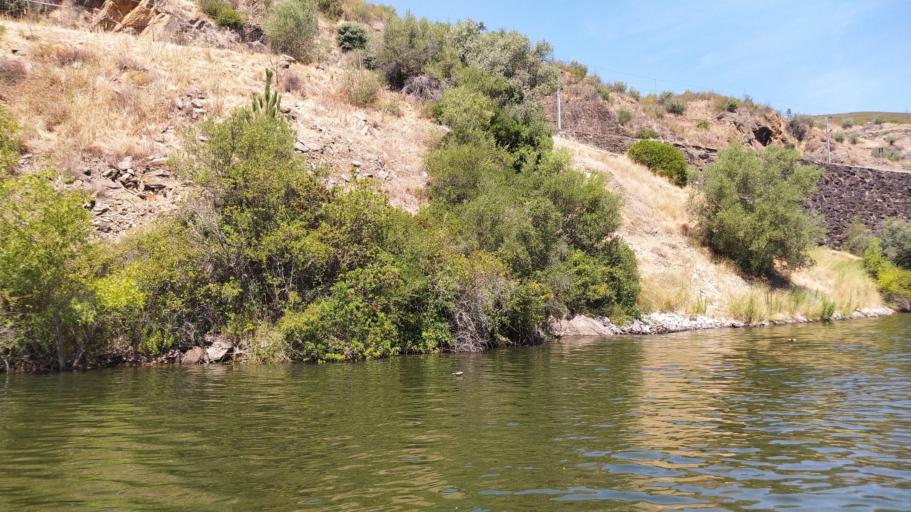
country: PT
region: Portalegre
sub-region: Nisa
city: Nisa
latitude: 39.6404
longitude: -7.6983
